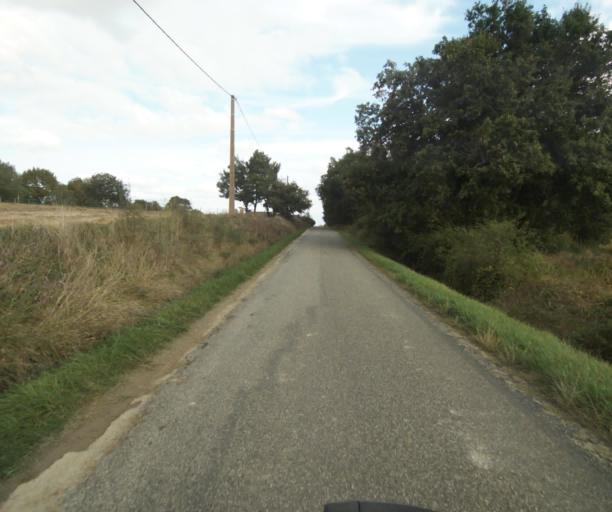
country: FR
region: Midi-Pyrenees
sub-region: Departement du Tarn-et-Garonne
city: Verdun-sur-Garonne
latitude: 43.8400
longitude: 1.1314
